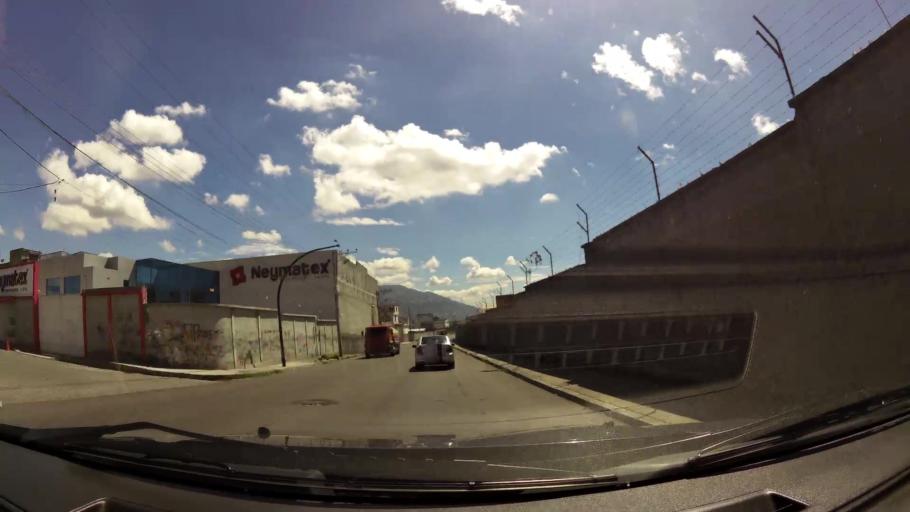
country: EC
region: Pichincha
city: Quito
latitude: -0.2987
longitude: -78.5443
